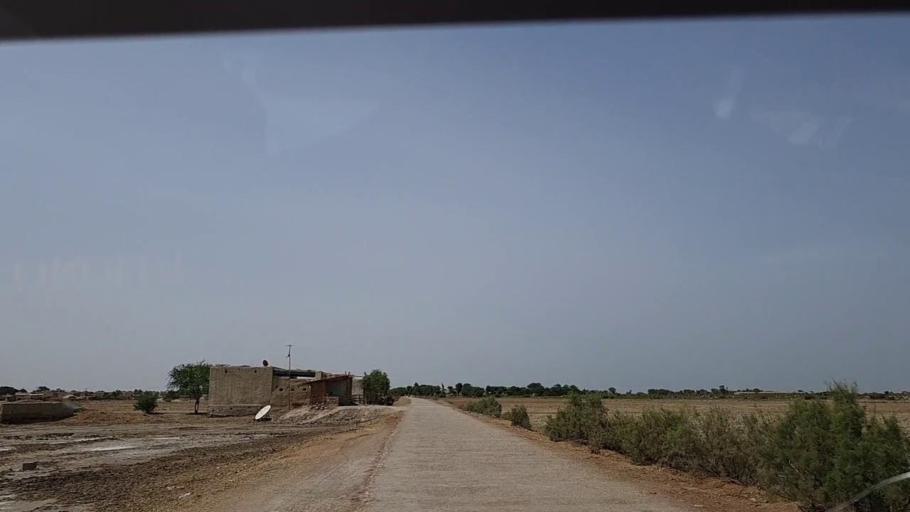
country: PK
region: Sindh
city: Johi
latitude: 26.7770
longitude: 67.6201
